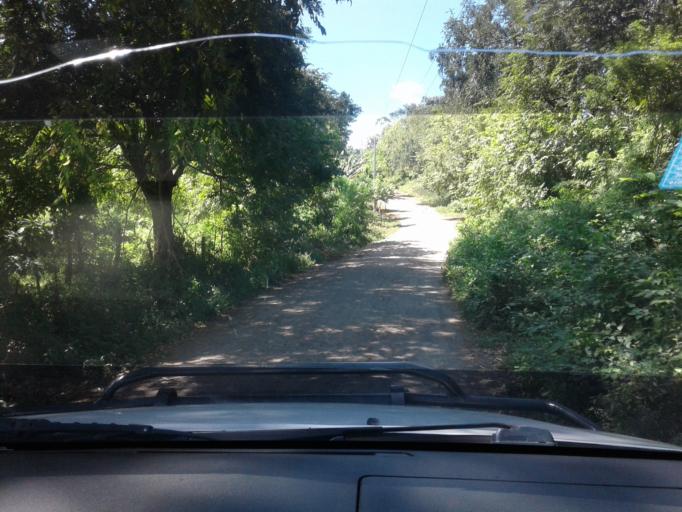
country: NI
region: Rivas
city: Altagracia
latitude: 11.4840
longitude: -85.5434
